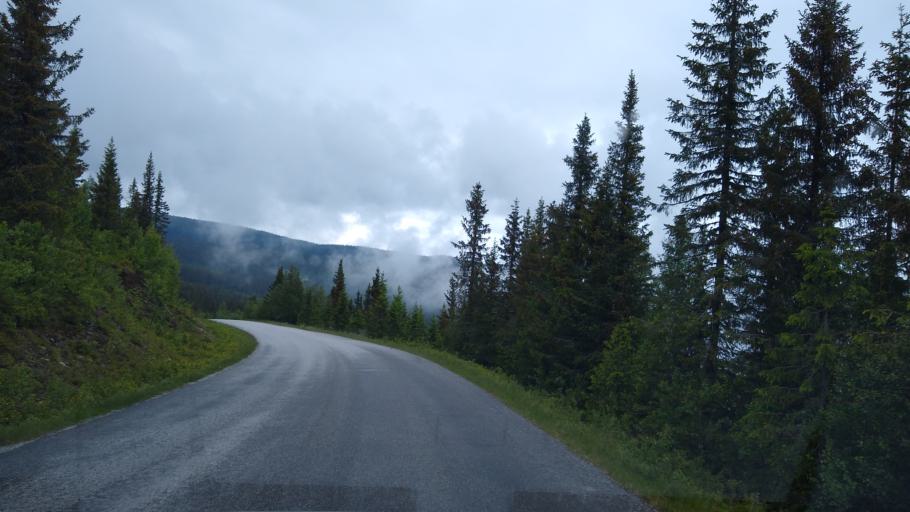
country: NO
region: Oppland
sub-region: Ringebu
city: Ringebu
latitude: 61.4825
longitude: 10.1220
